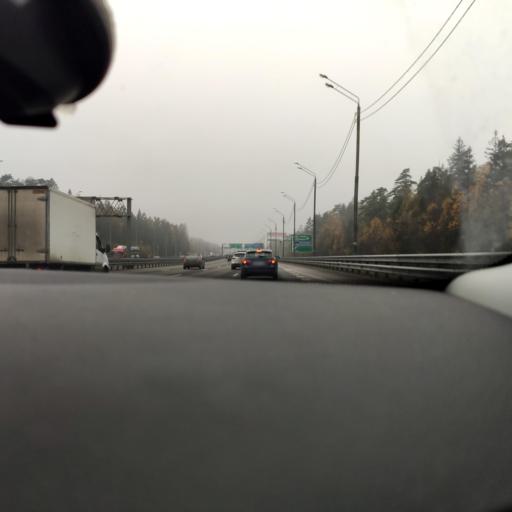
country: RU
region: Moskovskaya
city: Petrovo-Dal'neye
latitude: 55.7793
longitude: 37.1787
